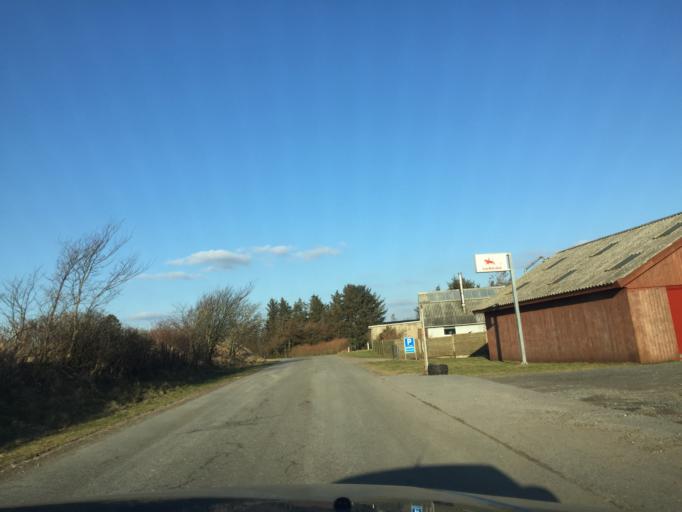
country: DK
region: Central Jutland
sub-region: Holstebro Kommune
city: Vinderup
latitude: 56.5817
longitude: 8.8073
